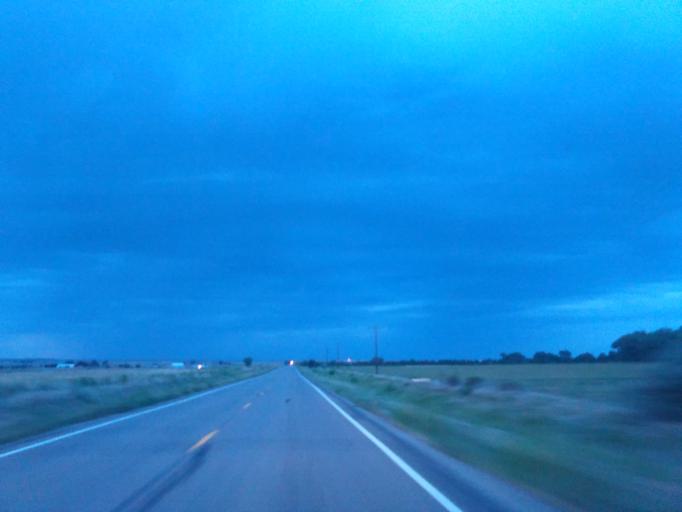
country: US
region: Colorado
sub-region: Las Animas County
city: Trinidad
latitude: 37.2677
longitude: -104.3505
